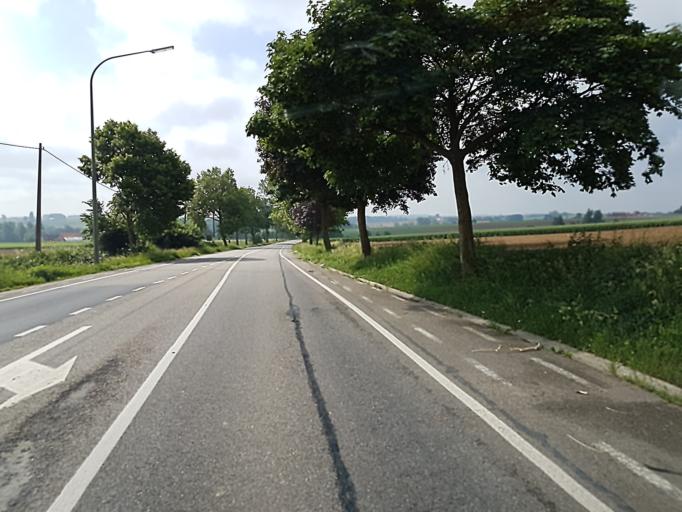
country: BE
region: Wallonia
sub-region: Province du Hainaut
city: Enghien
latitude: 50.6363
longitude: 4.0486
